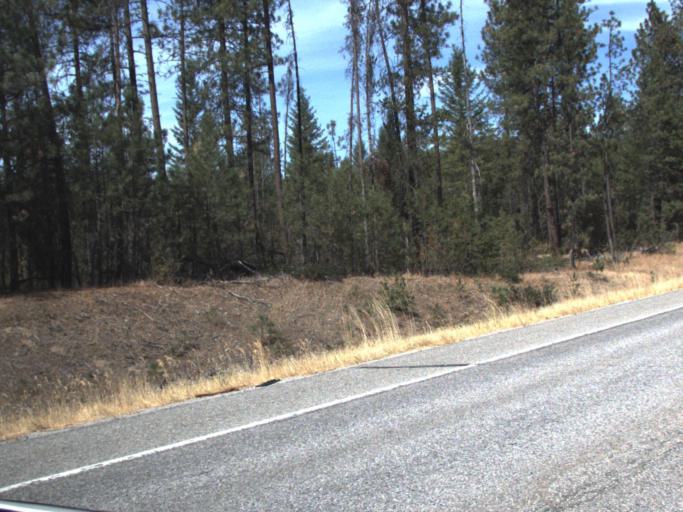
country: US
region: Washington
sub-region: Stevens County
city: Chewelah
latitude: 48.0896
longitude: -117.6345
